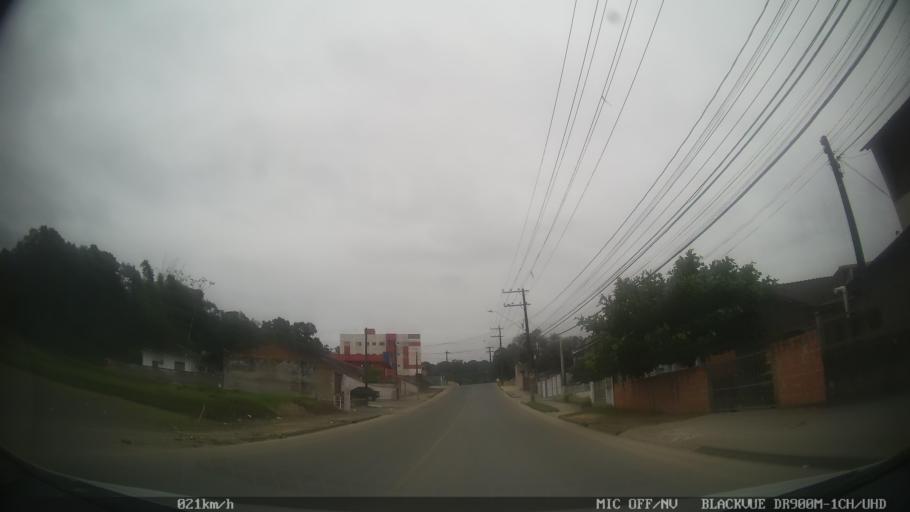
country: BR
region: Santa Catarina
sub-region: Joinville
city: Joinville
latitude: -26.3669
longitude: -48.8463
